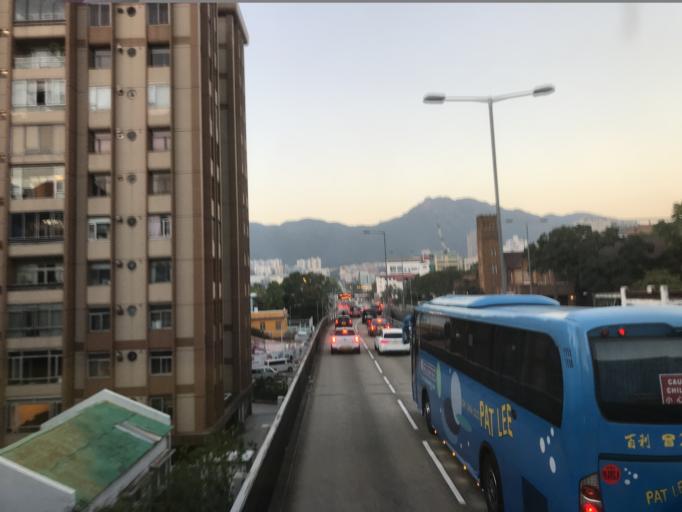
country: HK
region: Kowloon City
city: Kowloon
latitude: 22.3262
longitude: 114.1783
